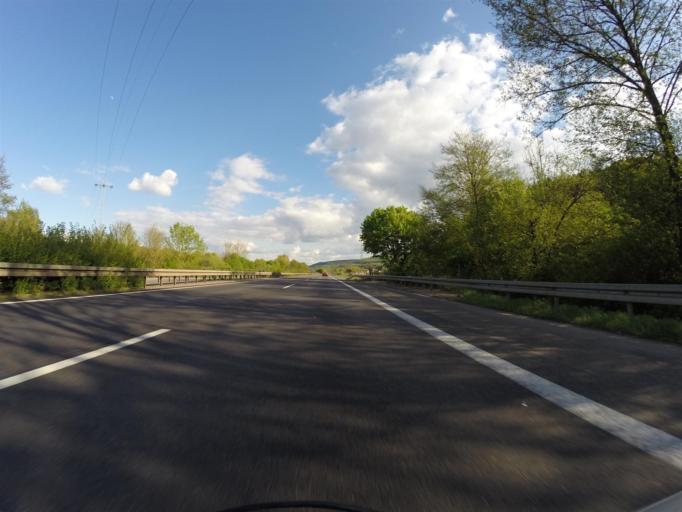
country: DE
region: Saarland
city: Merzig
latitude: 49.4277
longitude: 6.6300
